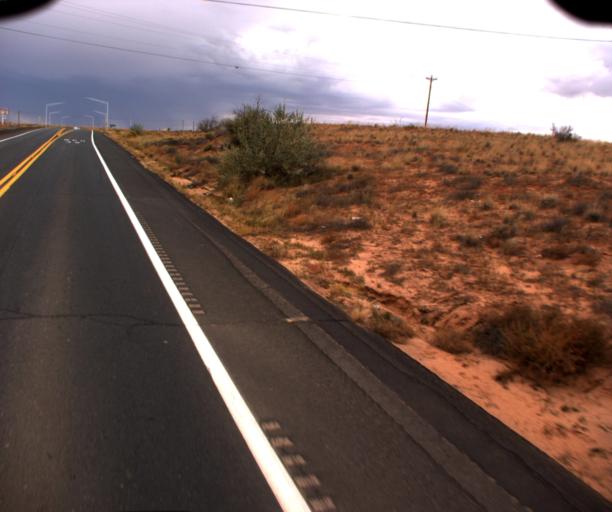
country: US
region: Arizona
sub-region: Coconino County
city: Kaibito
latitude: 36.3204
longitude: -110.9439
